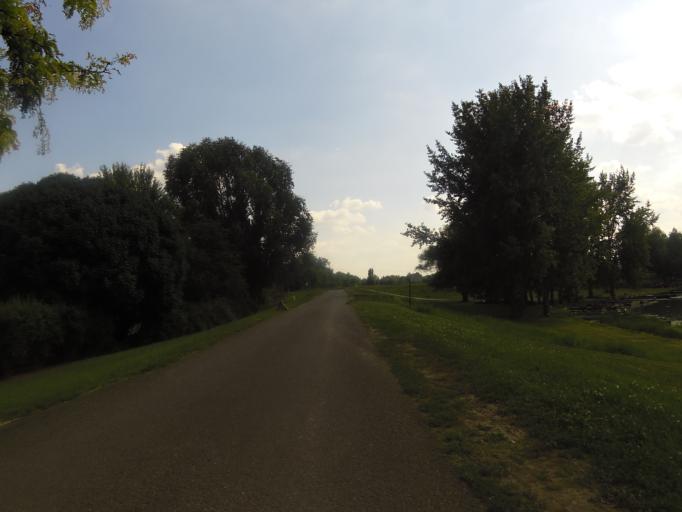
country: HU
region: Jasz-Nagykun-Szolnok
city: Tiszafured
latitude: 47.6097
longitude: 20.7228
